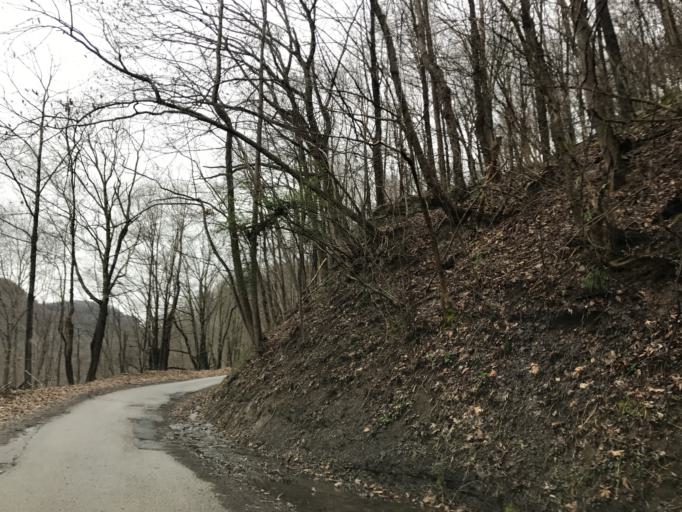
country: US
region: West Virginia
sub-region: Fayette County
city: Fayetteville
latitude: 38.0671
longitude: -81.0835
